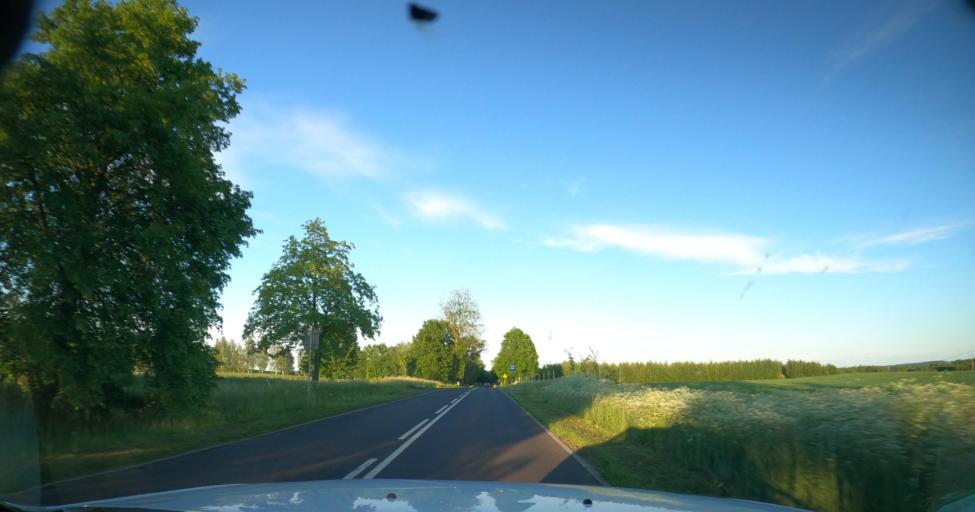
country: PL
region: Warmian-Masurian Voivodeship
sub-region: Powiat lidzbarski
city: Lidzbark Warminski
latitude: 54.1449
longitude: 20.4923
